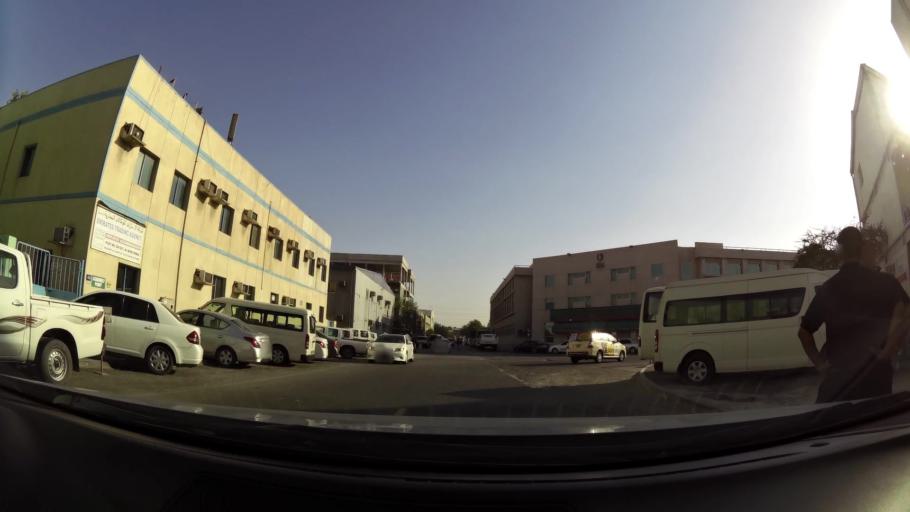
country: AE
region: Dubai
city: Dubai
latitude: 25.1308
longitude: 55.2521
